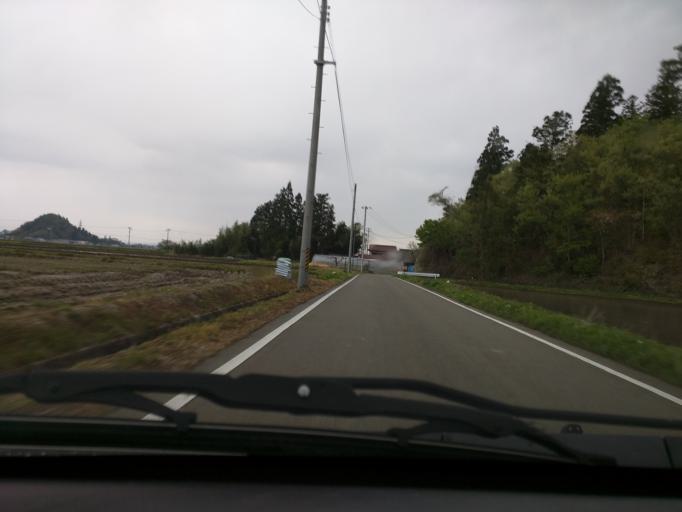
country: JP
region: Fukushima
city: Kitakata
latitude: 37.4321
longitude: 139.8879
